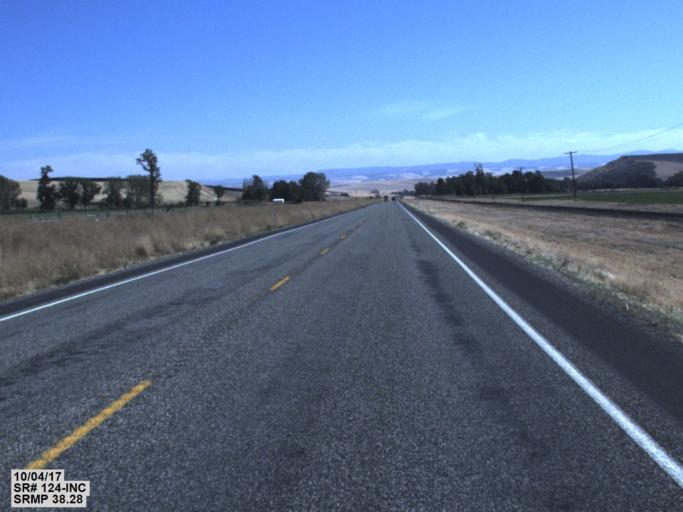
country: US
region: Washington
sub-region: Walla Walla County
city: Waitsburg
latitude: 46.2952
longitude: -118.2713
